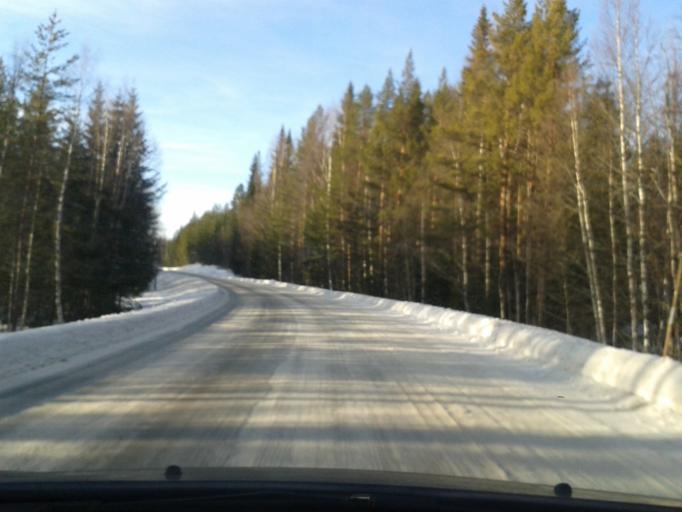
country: SE
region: Vaesternorrland
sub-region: OErnskoeldsviks Kommun
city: Bredbyn
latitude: 63.7422
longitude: 17.7406
